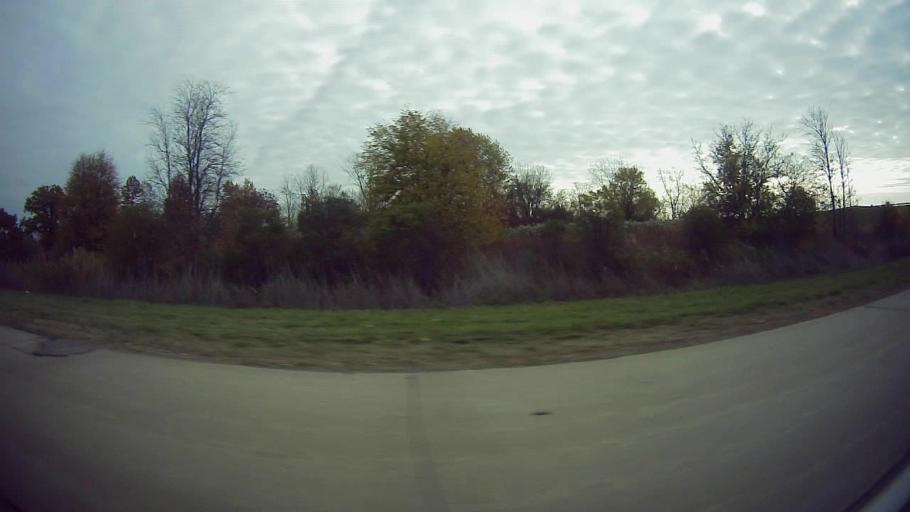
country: US
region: Michigan
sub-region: Wayne County
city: Woodhaven
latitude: 42.1716
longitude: -83.2431
